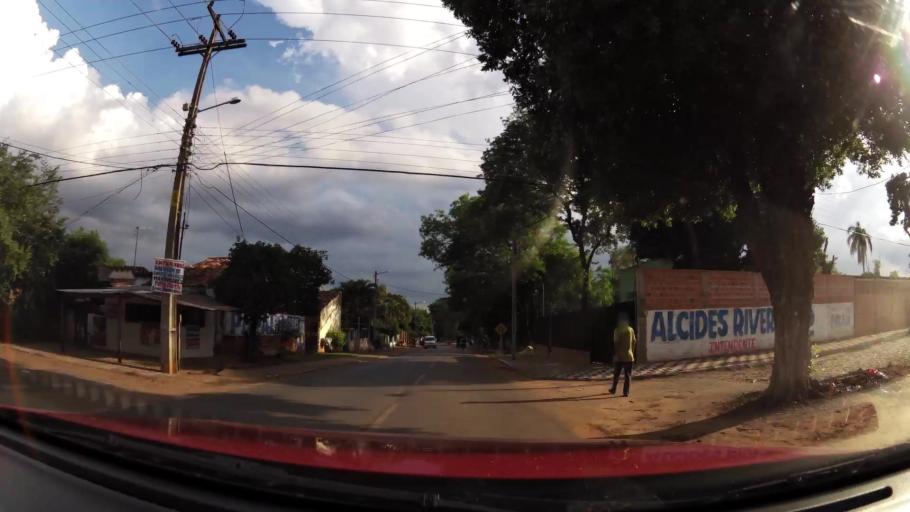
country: PY
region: Central
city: Fernando de la Mora
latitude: -25.3474
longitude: -57.5524
